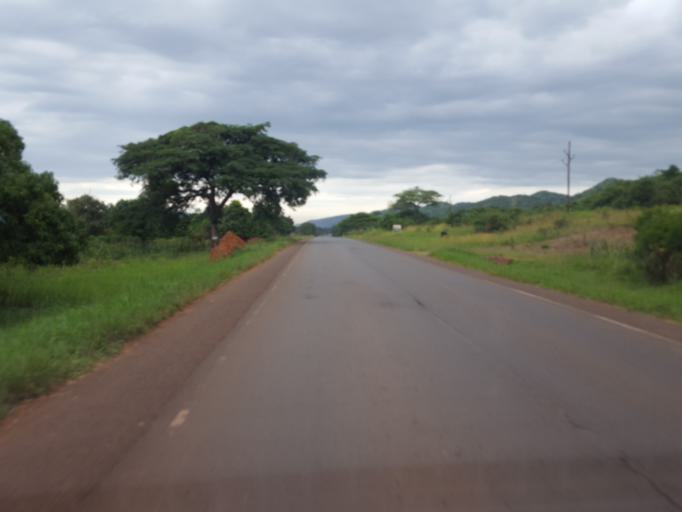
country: UG
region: Central Region
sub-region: Kiboga District
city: Kiboga
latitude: 0.8629
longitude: 31.8604
